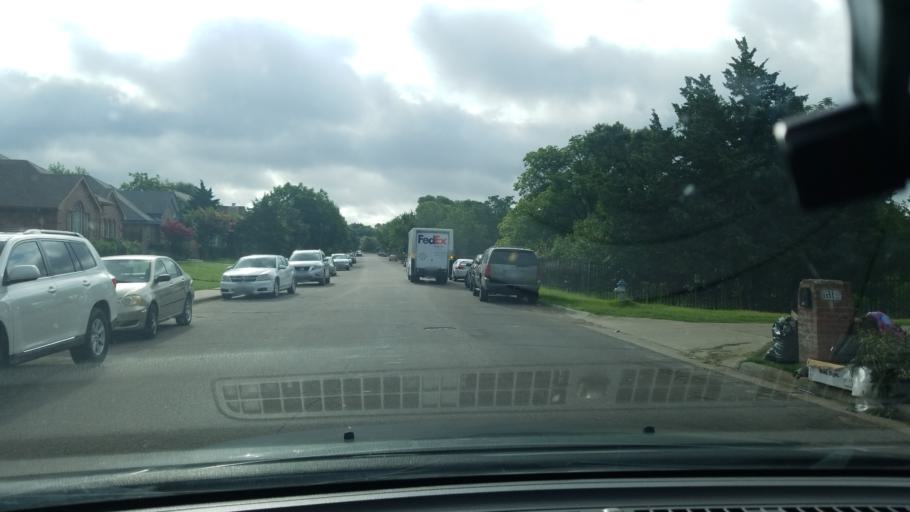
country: US
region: Texas
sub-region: Dallas County
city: Mesquite
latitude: 32.8133
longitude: -96.6824
